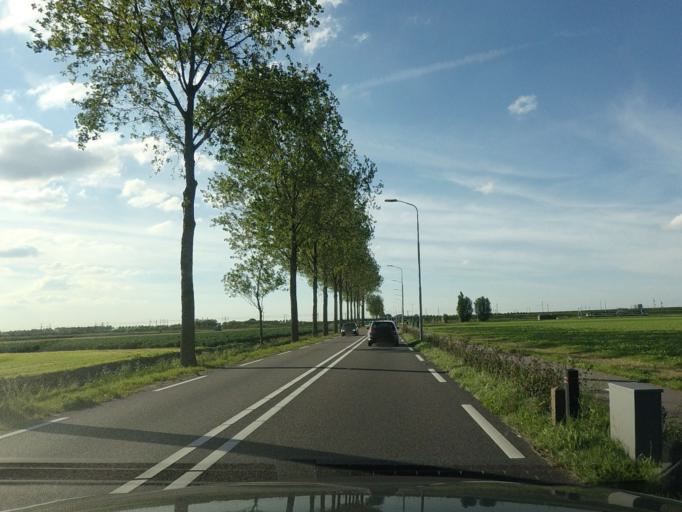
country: NL
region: North Holland
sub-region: Gemeente Haarlemmermeer
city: Hoofddorp
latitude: 52.2765
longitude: 4.6797
